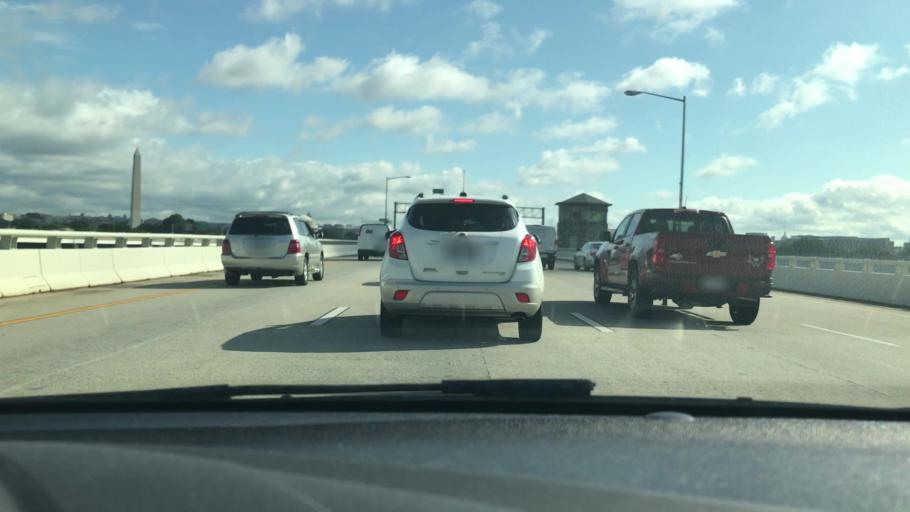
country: US
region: Washington, D.C.
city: Washington, D.C.
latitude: 38.8739
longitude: -77.0424
